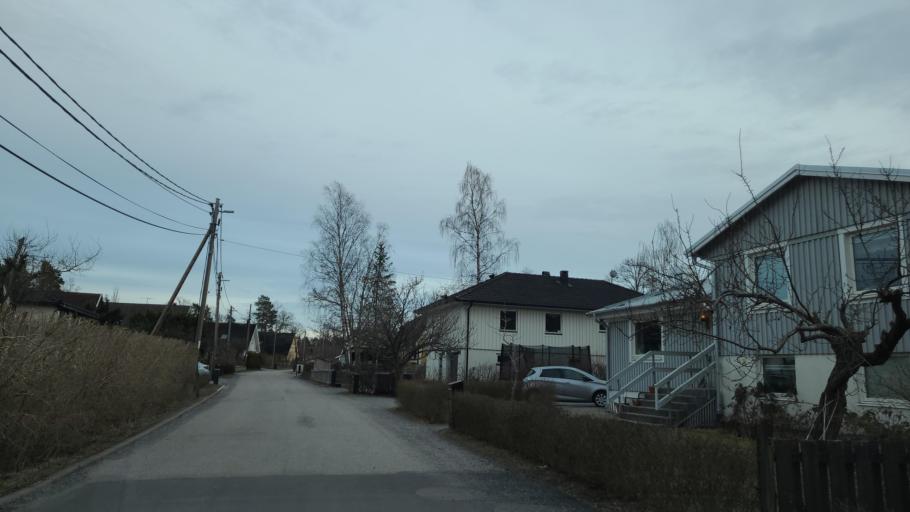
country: SE
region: Stockholm
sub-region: Nacka Kommun
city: Boo
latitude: 59.3203
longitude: 18.2630
